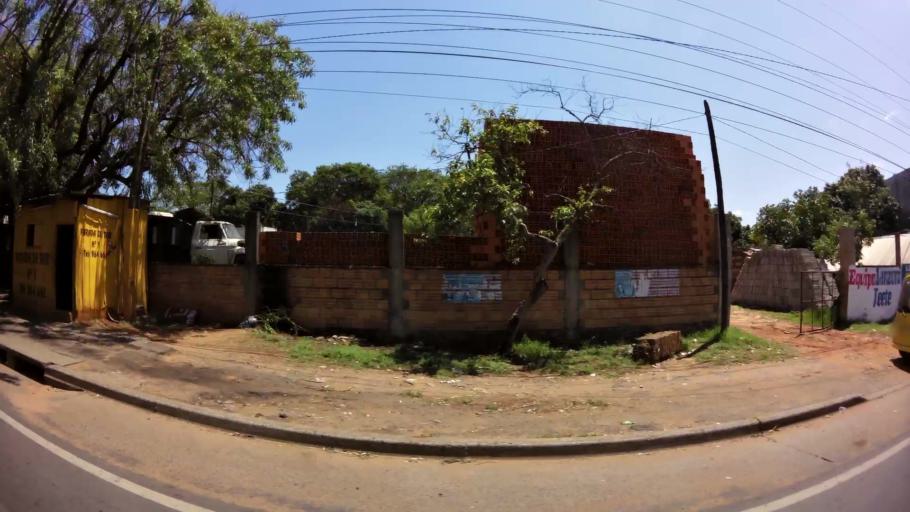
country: PY
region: Central
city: Nemby
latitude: -25.4051
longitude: -57.5430
